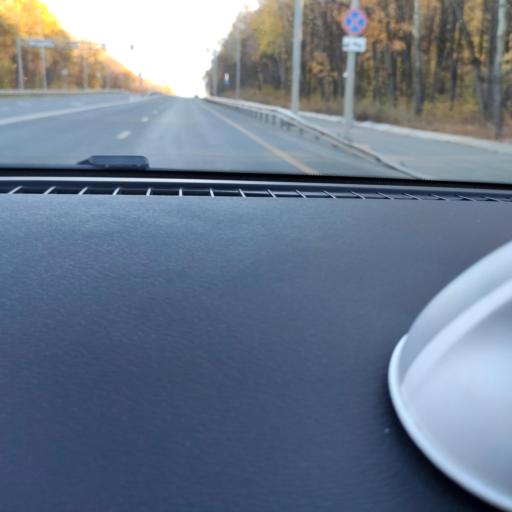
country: RU
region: Samara
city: Petra-Dubrava
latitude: 53.2869
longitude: 50.2498
